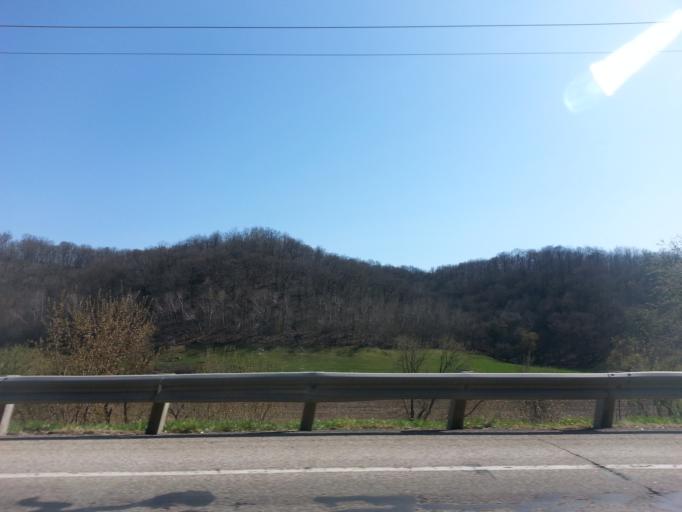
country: US
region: Wisconsin
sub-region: Pepin County
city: Durand
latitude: 44.6405
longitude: -92.0979
